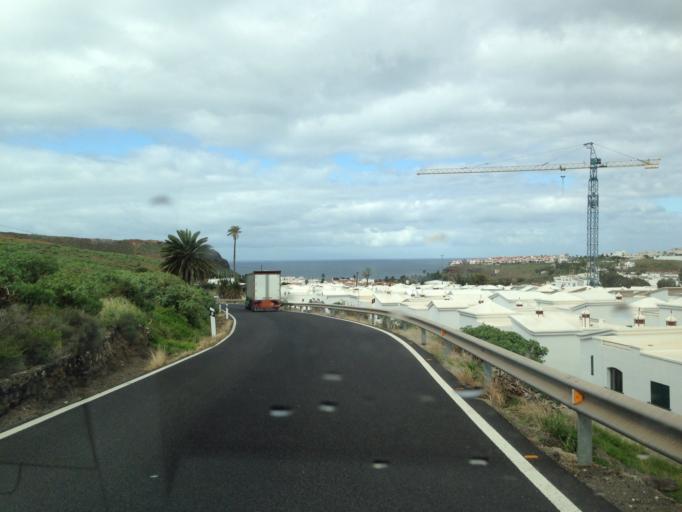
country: ES
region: Canary Islands
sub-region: Provincia de Las Palmas
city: Agaete
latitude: 28.0966
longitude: -15.7008
